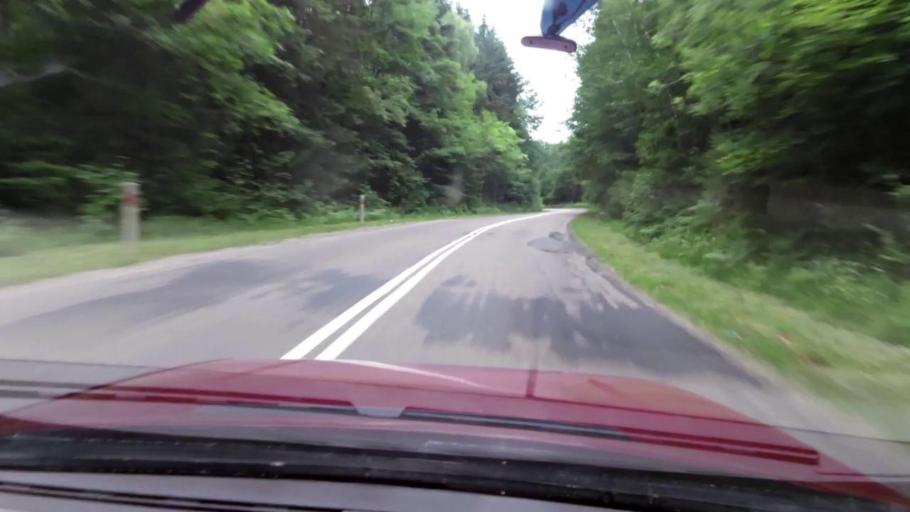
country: PL
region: West Pomeranian Voivodeship
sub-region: Powiat koszalinski
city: Sianow
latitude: 54.1887
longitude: 16.2790
